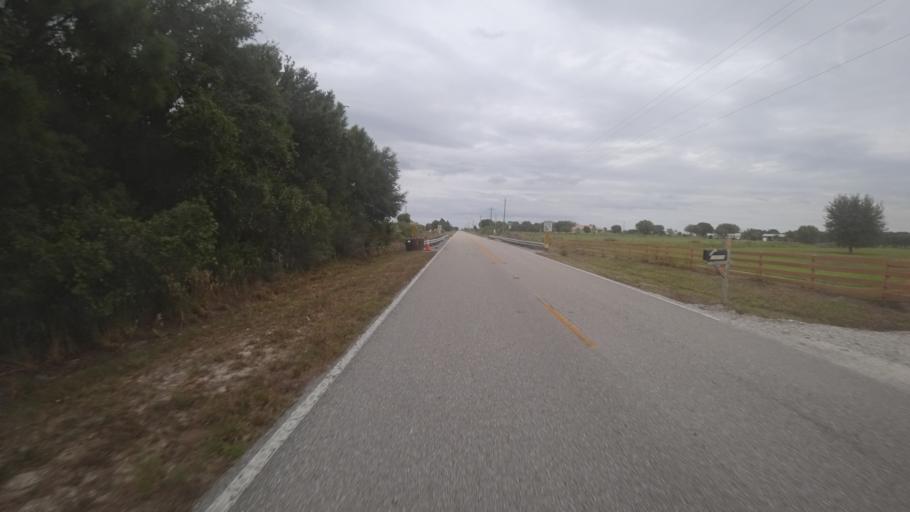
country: US
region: Florida
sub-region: Sarasota County
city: Warm Mineral Springs
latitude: 27.2768
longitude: -82.1958
